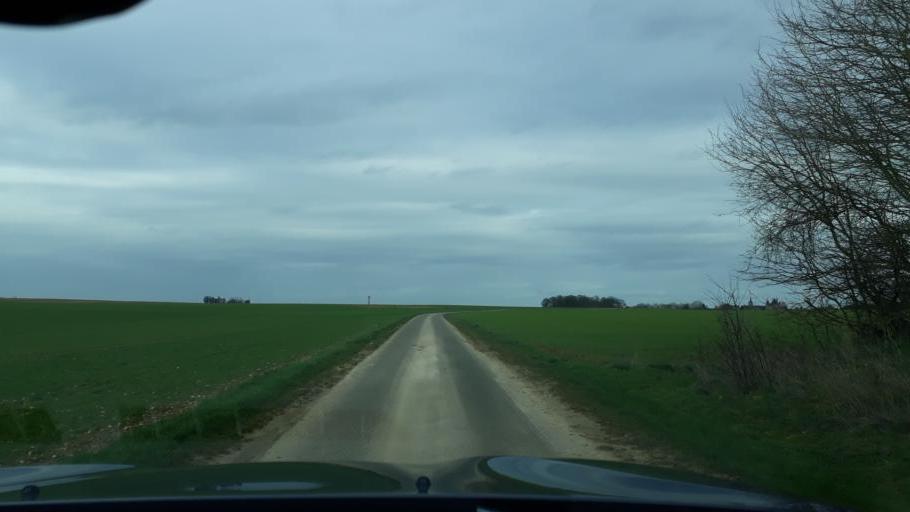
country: FR
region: Centre
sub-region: Departement du Loir-et-Cher
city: Mer
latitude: 47.7718
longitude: 1.4292
